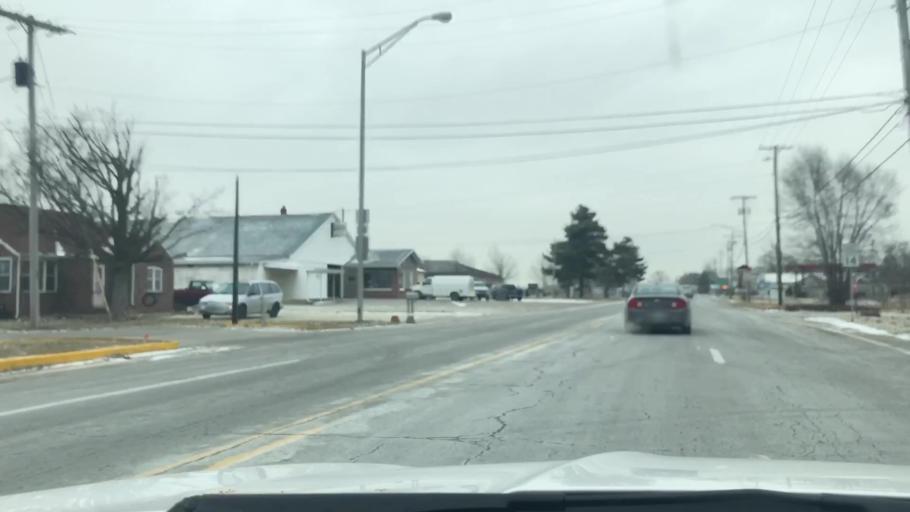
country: US
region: Indiana
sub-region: Fulton County
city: Rochester
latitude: 41.0617
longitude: -86.1917
